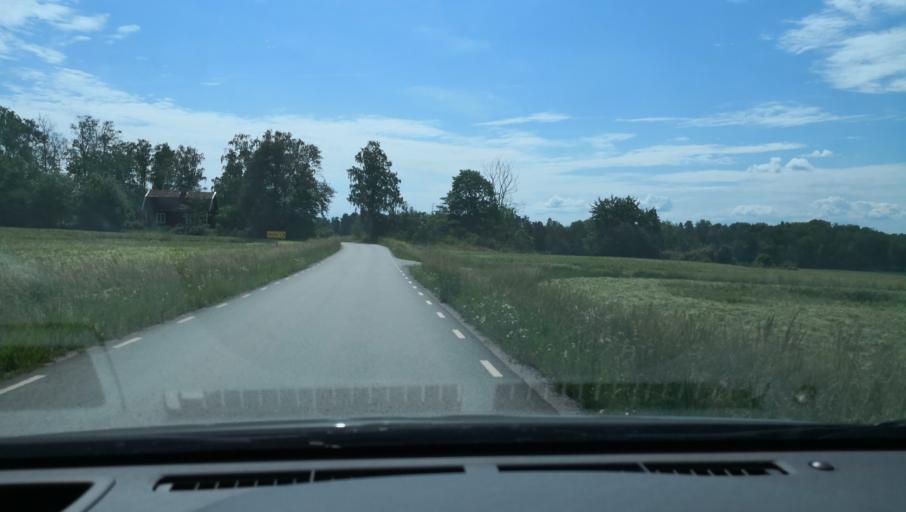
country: SE
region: Uppsala
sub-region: Habo Kommun
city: Balsta
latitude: 59.6856
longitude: 17.4634
